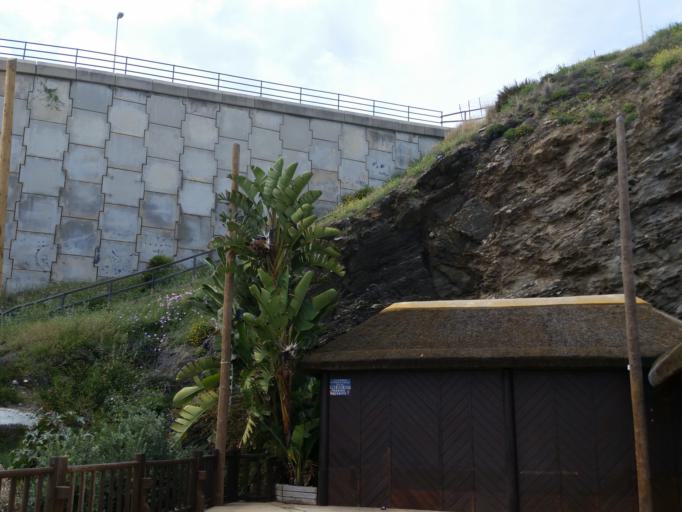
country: ES
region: Andalusia
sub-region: Provincia de Malaga
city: Benalmadena
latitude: 36.5804
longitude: -4.5398
